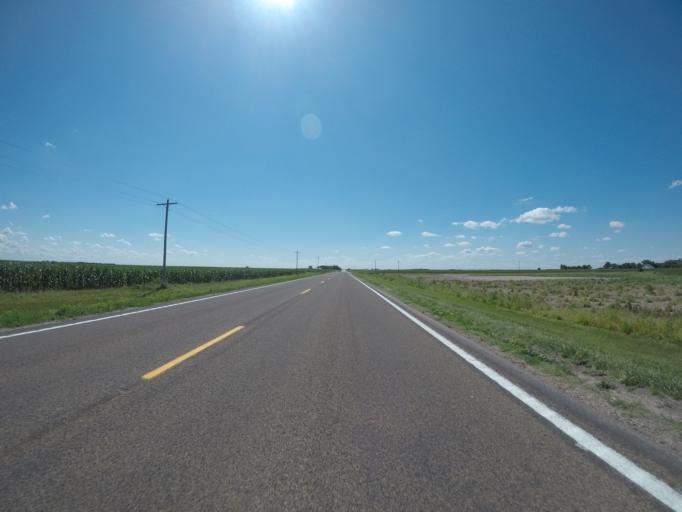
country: US
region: Nebraska
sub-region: Chase County
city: Imperial
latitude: 40.5377
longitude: -101.7206
